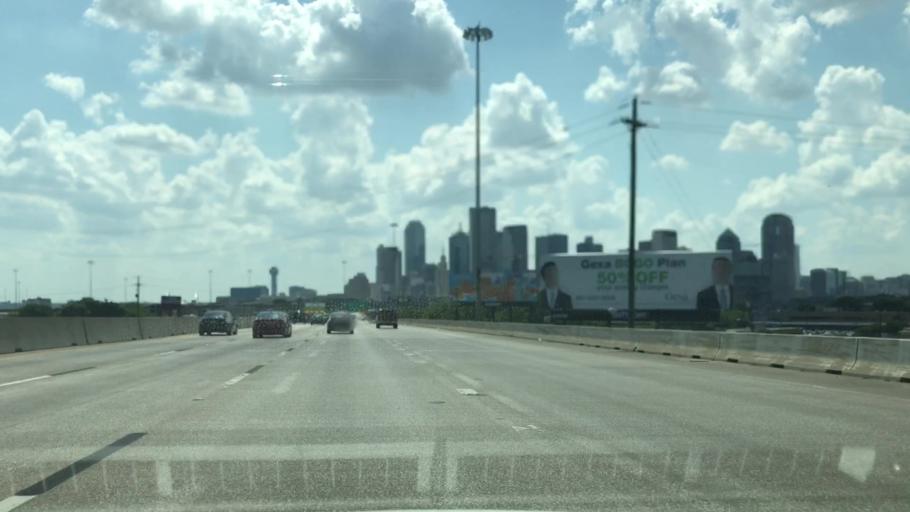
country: US
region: Texas
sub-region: Dallas County
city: Dallas
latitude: 32.7809
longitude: -96.7741
